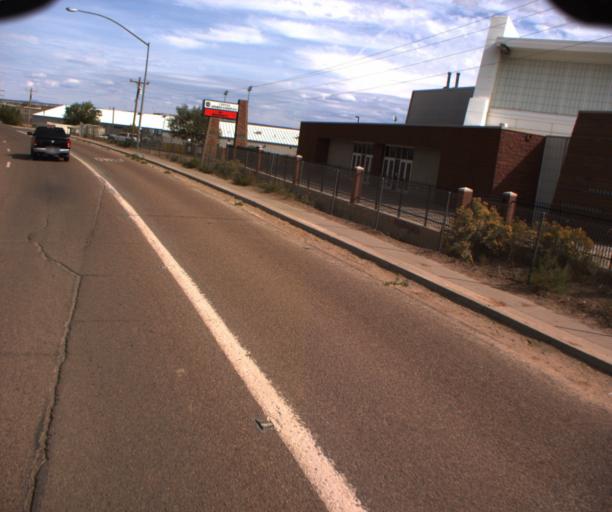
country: US
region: Arizona
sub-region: Apache County
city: Chinle
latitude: 36.1561
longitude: -109.5838
